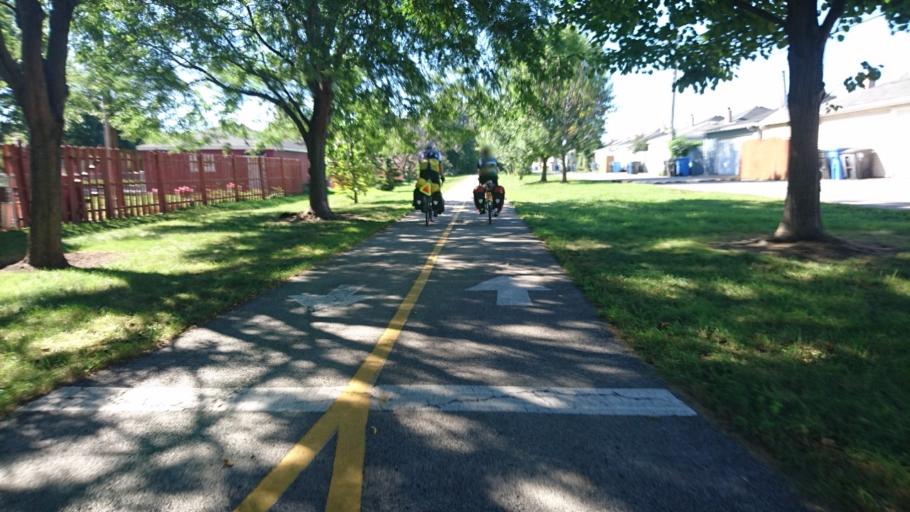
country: US
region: Indiana
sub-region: Lake County
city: Whiting
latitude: 41.6990
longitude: -87.5285
